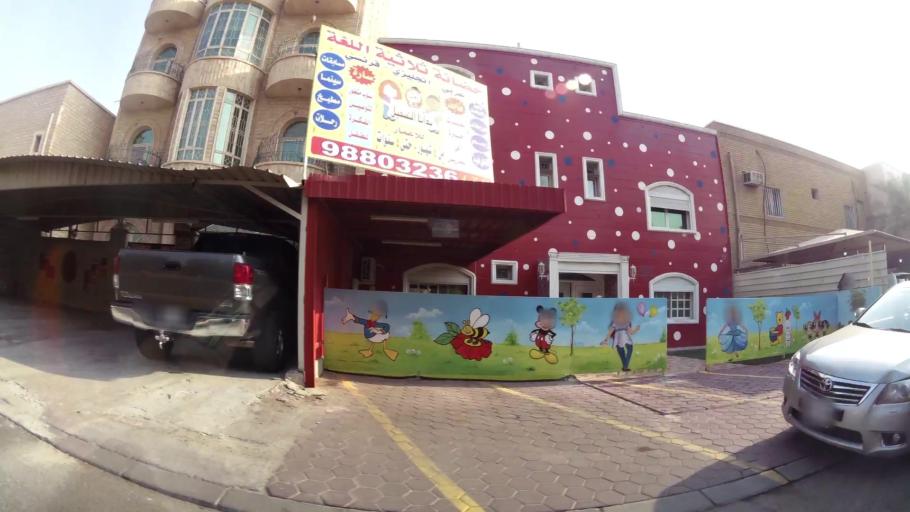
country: KW
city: Bayan
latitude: 29.2960
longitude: 48.0539
